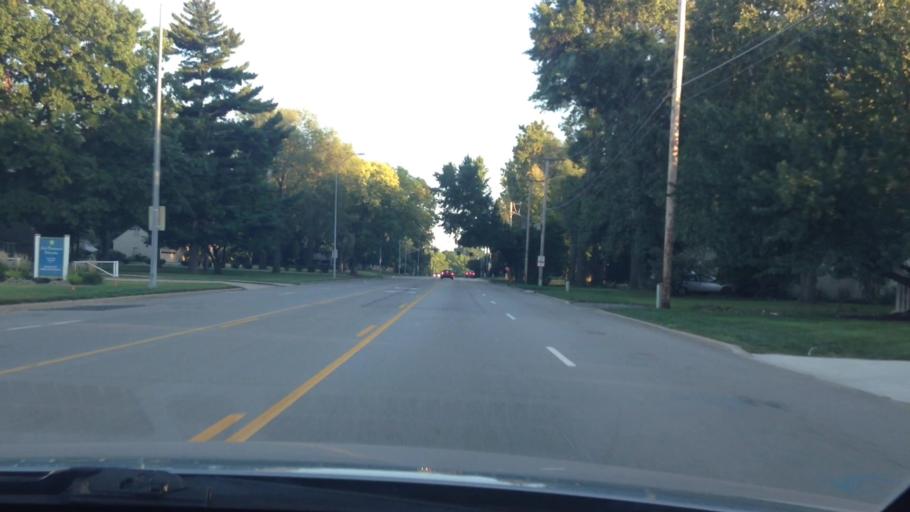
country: US
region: Kansas
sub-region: Johnson County
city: Leawood
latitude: 38.9314
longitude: -94.5950
